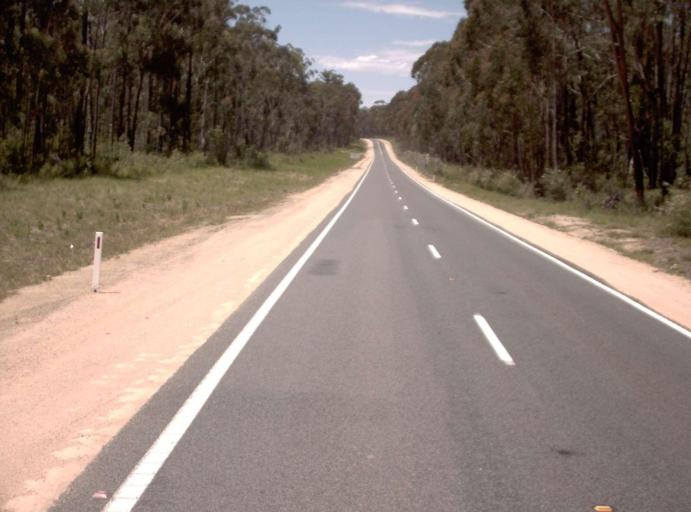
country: AU
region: Victoria
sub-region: East Gippsland
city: Lakes Entrance
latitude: -37.6780
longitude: 148.7806
